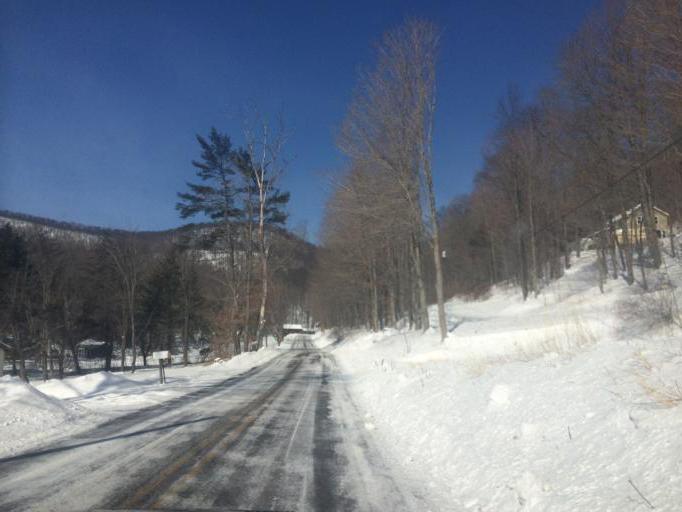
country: US
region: Pennsylvania
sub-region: Centre County
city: Stormstown
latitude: 40.8626
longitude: -78.0280
